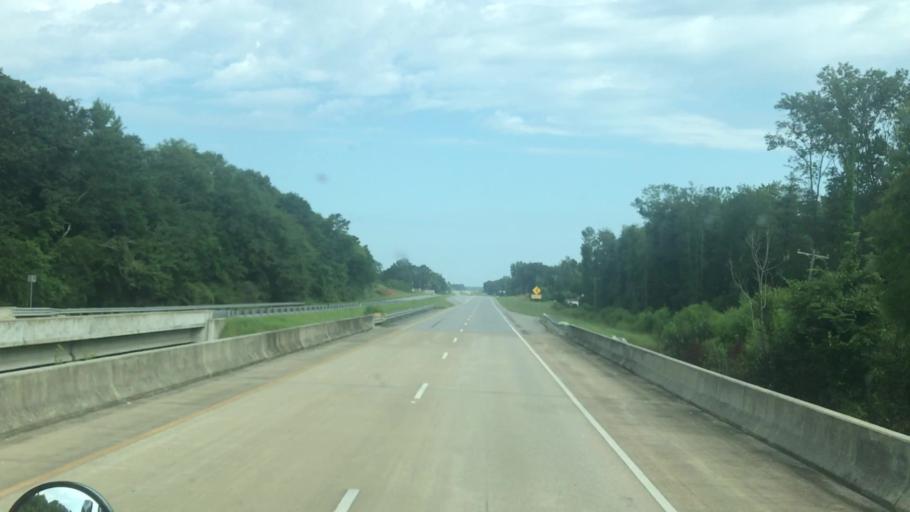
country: US
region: Georgia
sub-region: Early County
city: Blakely
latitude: 31.3329
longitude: -84.8962
